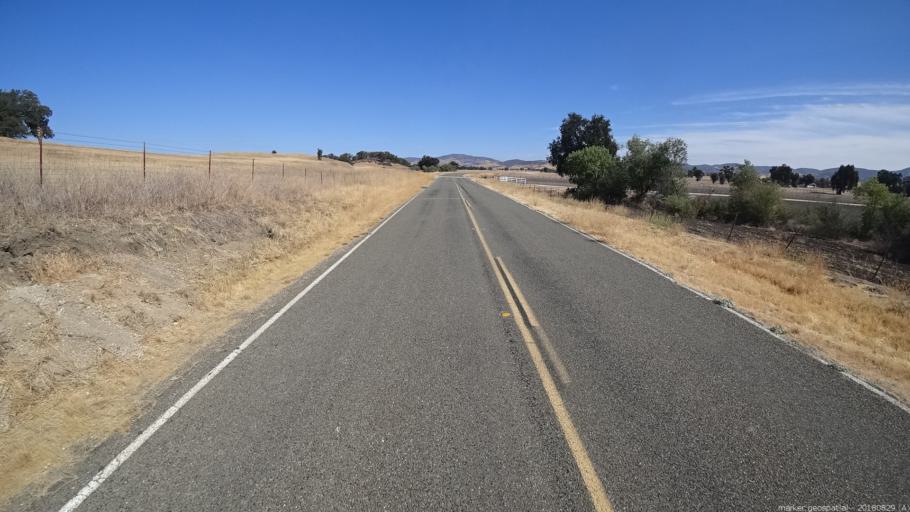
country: US
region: California
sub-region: San Luis Obispo County
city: Lake Nacimiento
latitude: 35.9187
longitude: -121.0842
